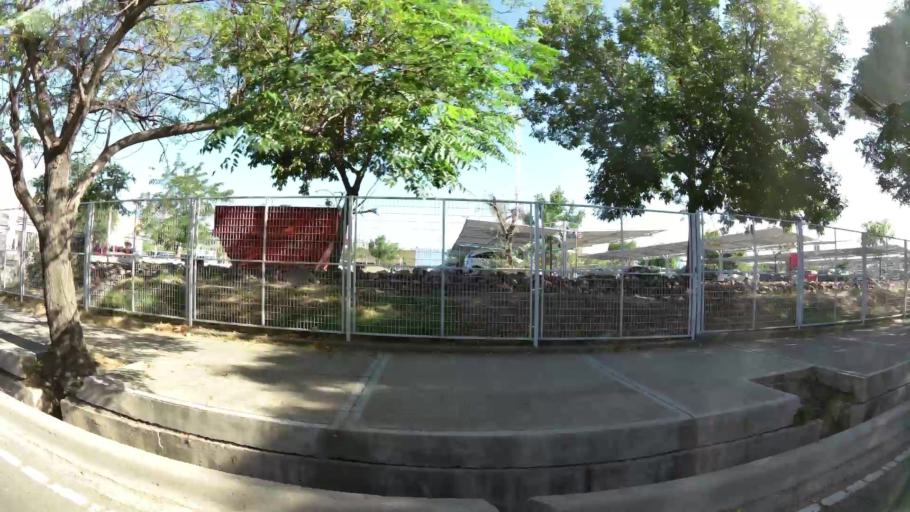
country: AR
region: Mendoza
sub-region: Departamento de Godoy Cruz
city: Godoy Cruz
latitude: -32.9142
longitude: -68.8252
